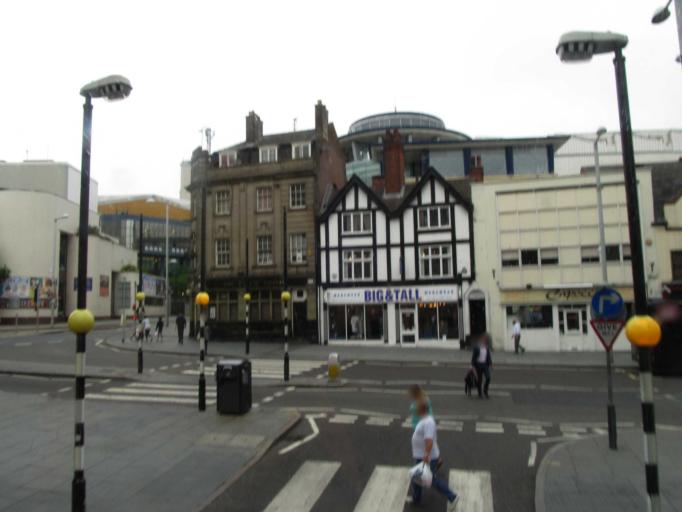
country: GB
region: England
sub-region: Nottingham
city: Nottingham
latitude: 52.9550
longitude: -1.1503
